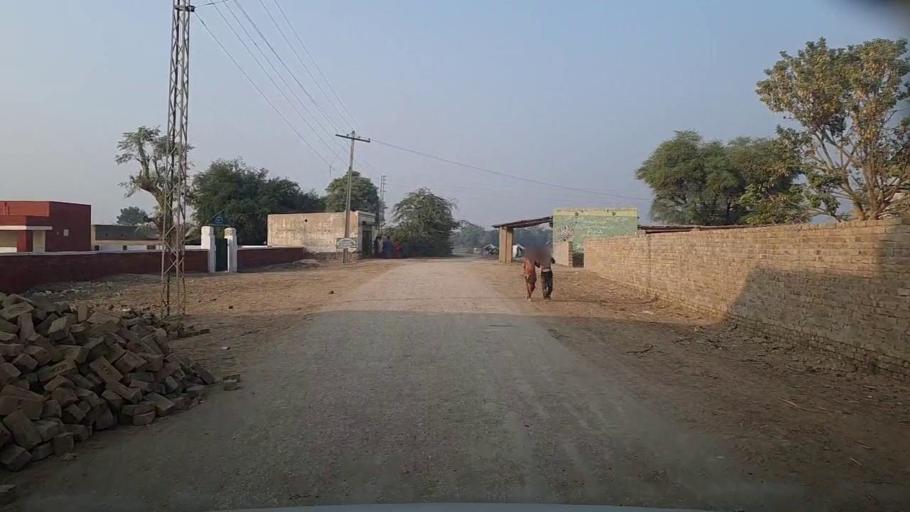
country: PK
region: Sindh
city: Kandiari
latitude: 27.0073
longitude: 68.4619
